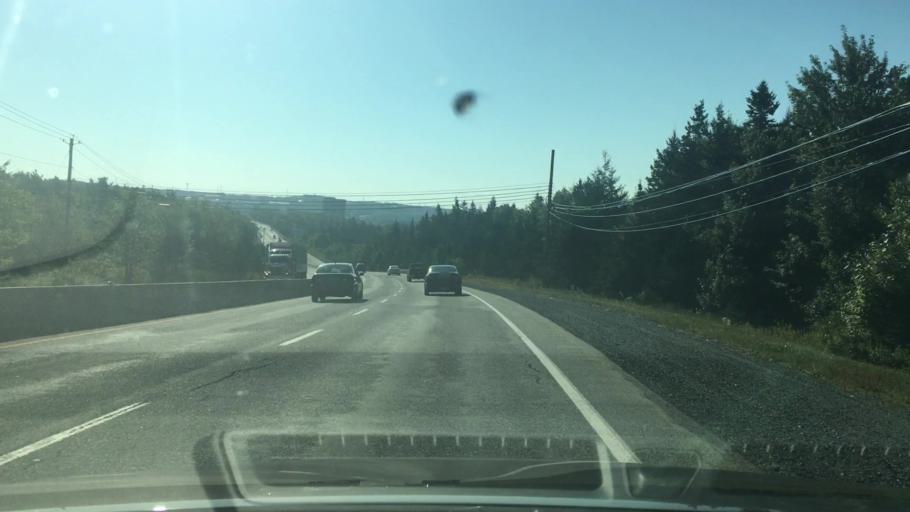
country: CA
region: Nova Scotia
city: Dartmouth
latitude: 44.7095
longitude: -63.6254
